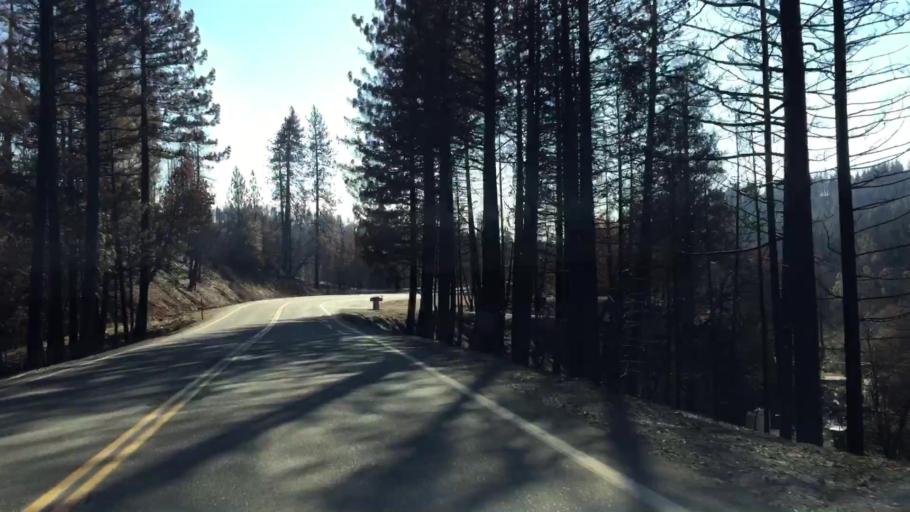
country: US
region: California
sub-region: Butte County
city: Magalia
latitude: 39.7307
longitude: -121.4943
